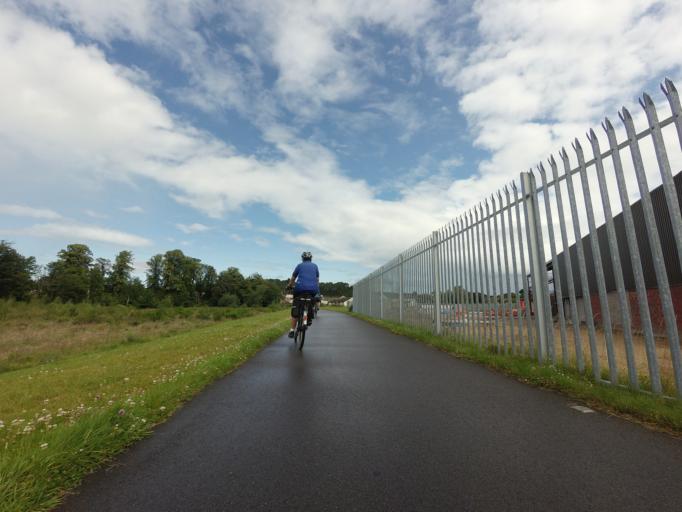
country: GB
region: Scotland
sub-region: Moray
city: Elgin
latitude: 57.6510
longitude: -3.2964
